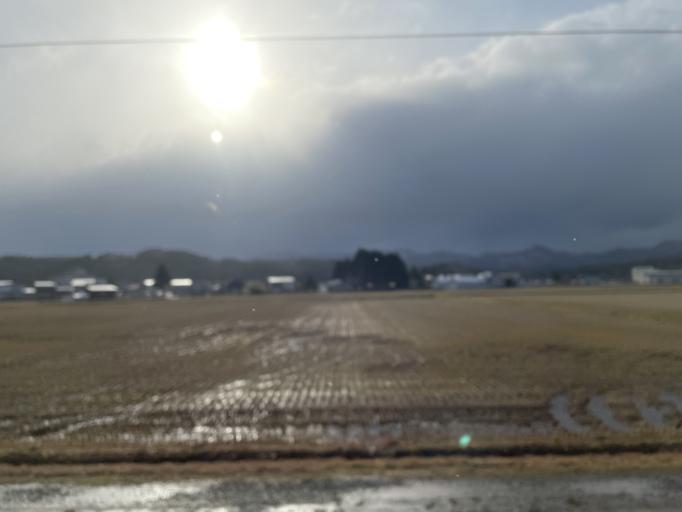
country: JP
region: Aomori
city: Aomori Shi
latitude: 41.0537
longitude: 140.5931
